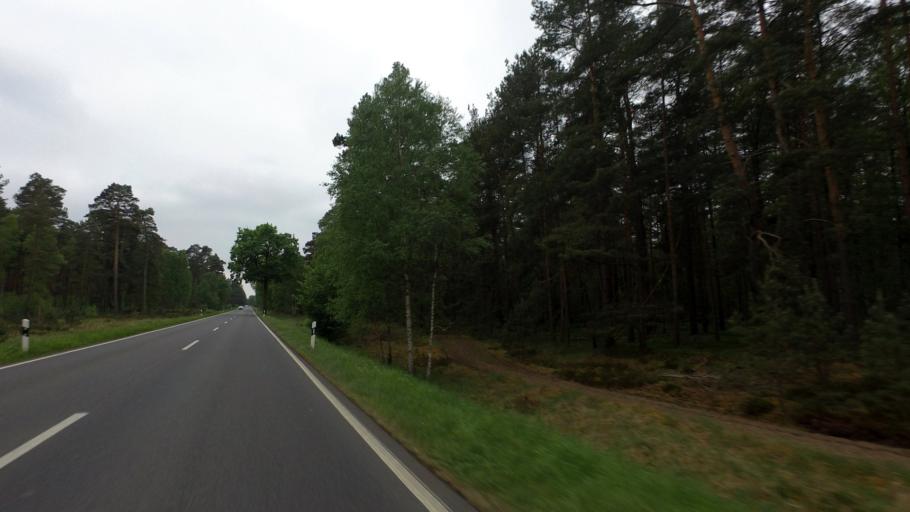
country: DE
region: Brandenburg
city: Marienwerder
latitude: 52.9641
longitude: 13.5716
